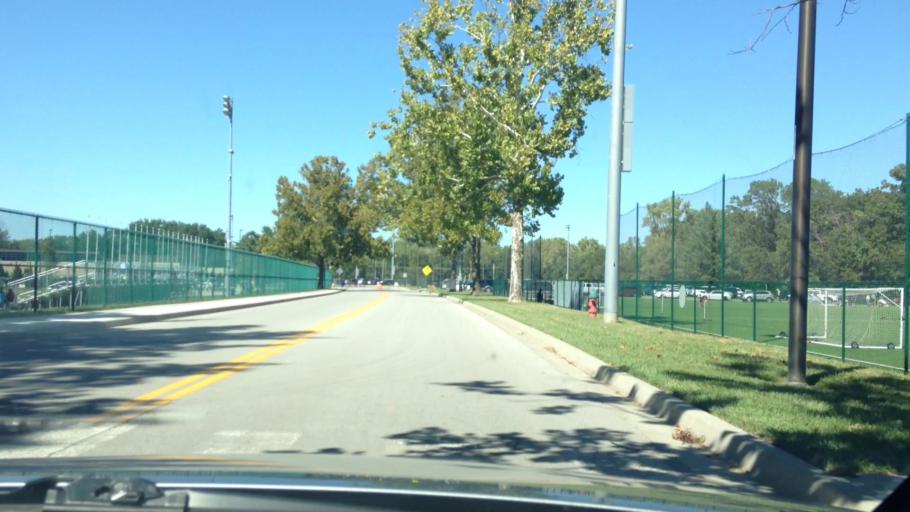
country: US
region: Missouri
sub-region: Jackson County
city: Raytown
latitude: 39.0108
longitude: -94.5192
